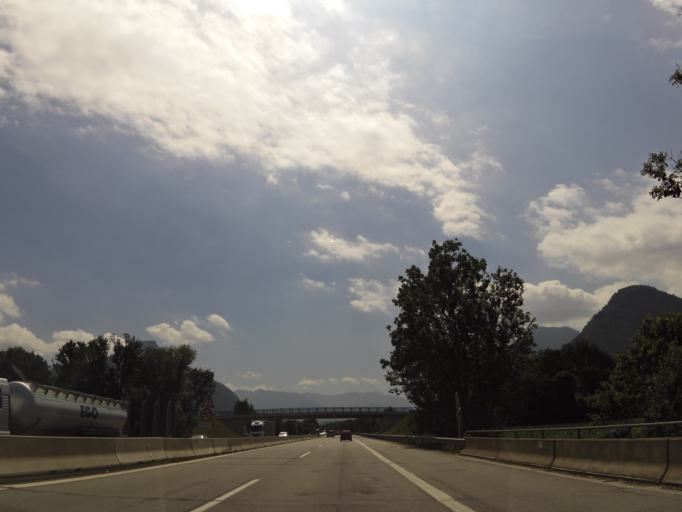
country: DE
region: Bavaria
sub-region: Upper Bavaria
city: Flintsbach
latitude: 47.7305
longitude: 12.1335
